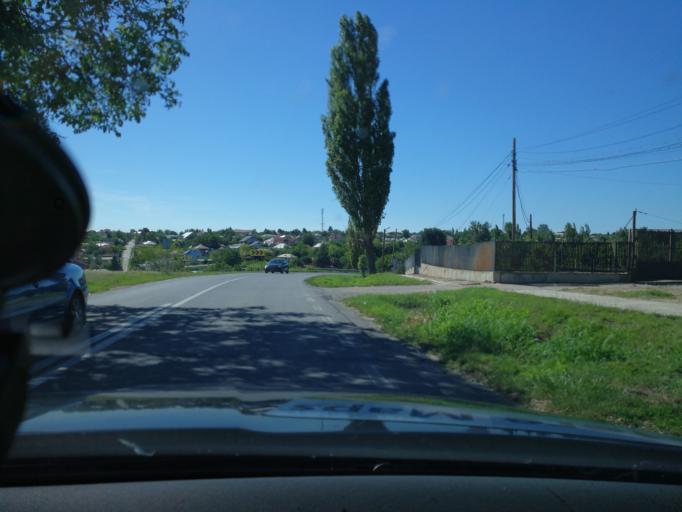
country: RO
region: Tulcea
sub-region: Oras Macin
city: Macin
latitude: 45.2404
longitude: 28.1489
